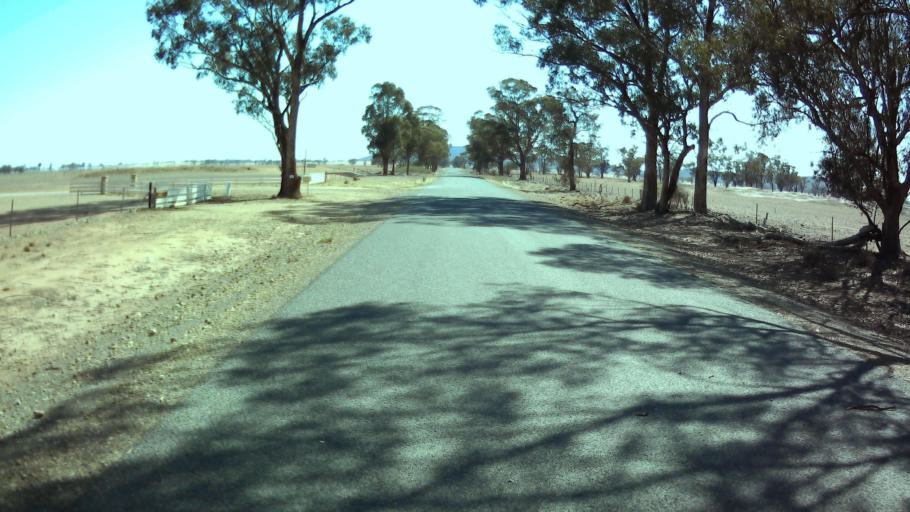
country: AU
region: New South Wales
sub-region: Weddin
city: Grenfell
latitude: -33.7166
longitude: 147.9048
